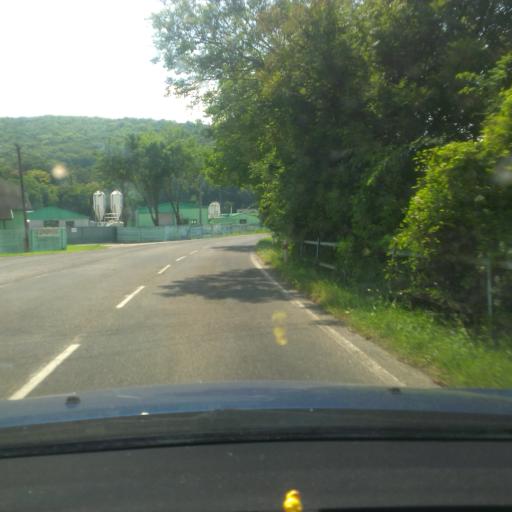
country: SK
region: Trnavsky
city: Hlohovec
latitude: 48.5068
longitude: 17.8278
